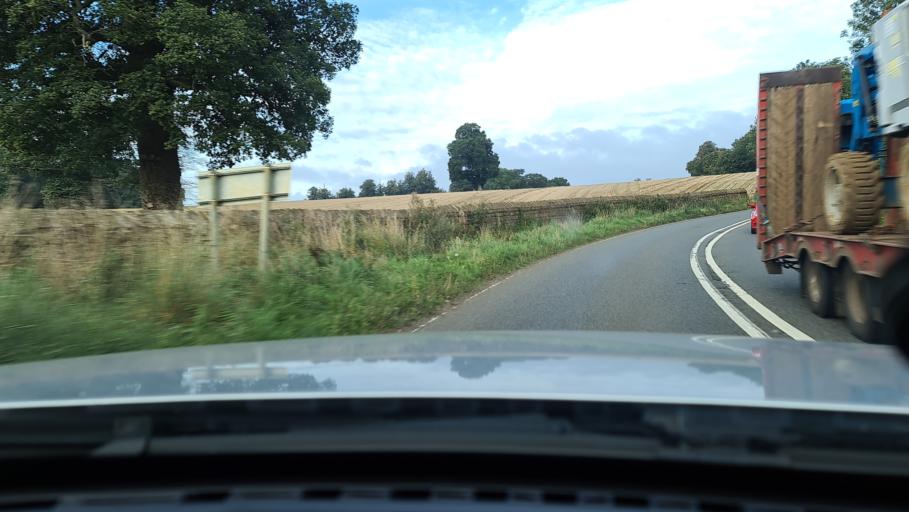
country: GB
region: England
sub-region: Oxfordshire
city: Hanwell
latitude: 52.0740
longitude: -1.3808
